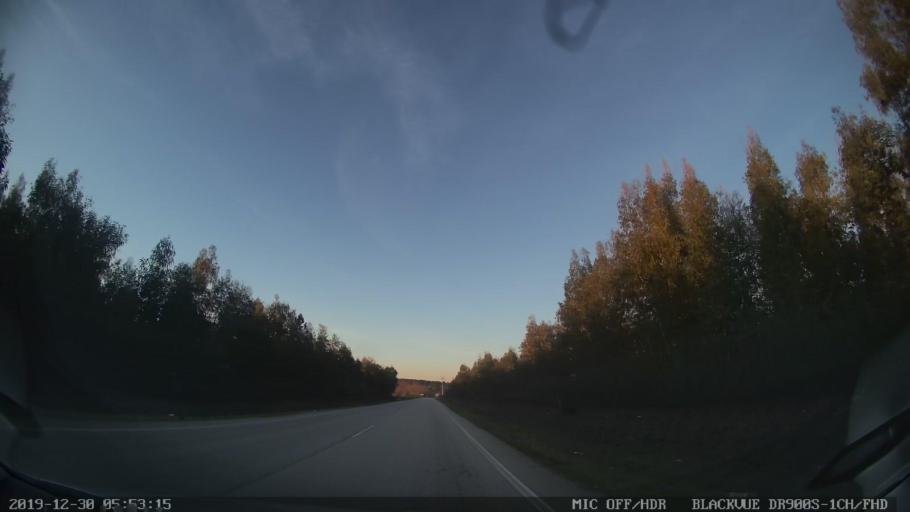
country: PT
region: Castelo Branco
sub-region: Idanha-A-Nova
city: Idanha-a-Nova
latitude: 40.0137
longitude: -7.2505
